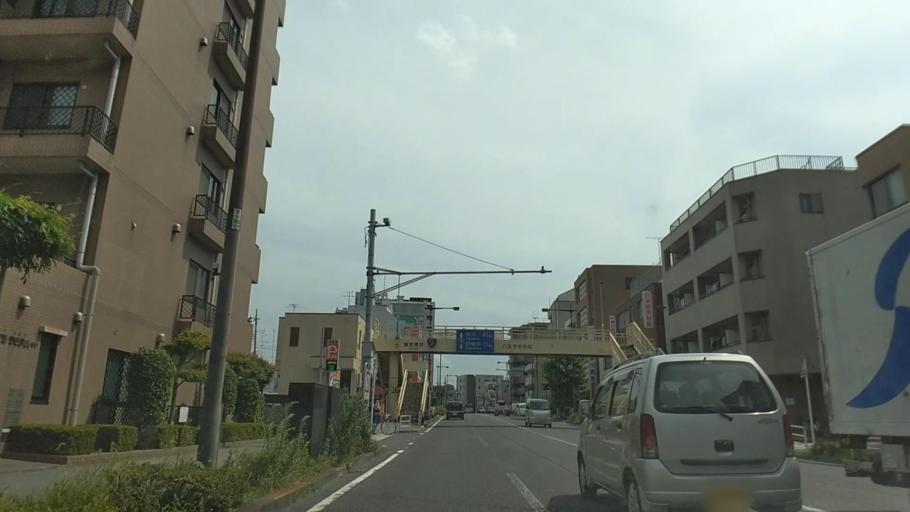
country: JP
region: Tokyo
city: Hachioji
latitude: 35.6560
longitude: 139.3330
